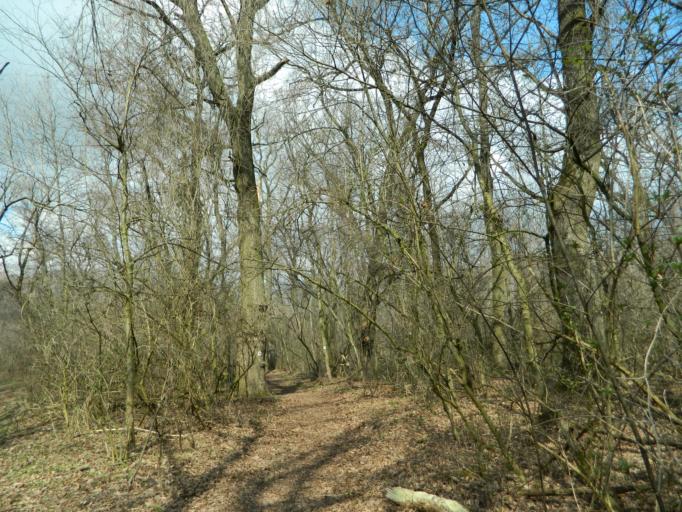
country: HU
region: Fejer
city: Sarszentmihaly
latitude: 47.1571
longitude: 18.3699
